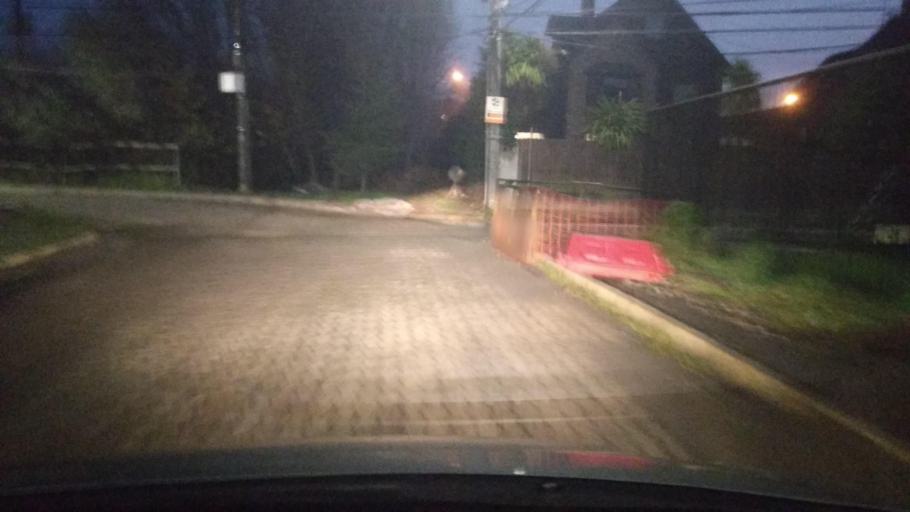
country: CL
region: Los Rios
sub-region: Provincia de Valdivia
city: Valdivia
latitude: -39.8168
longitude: -73.2566
